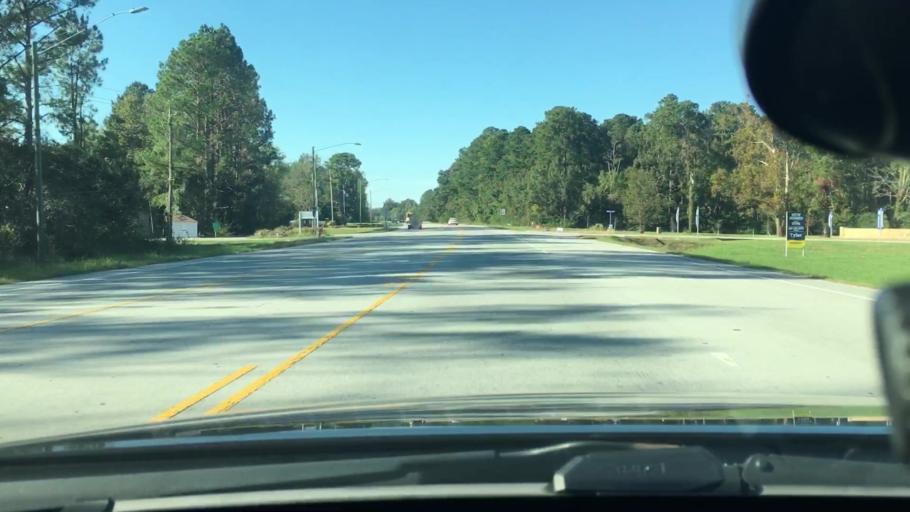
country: US
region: North Carolina
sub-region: Craven County
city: Trent Woods
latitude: 35.1513
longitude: -77.1096
